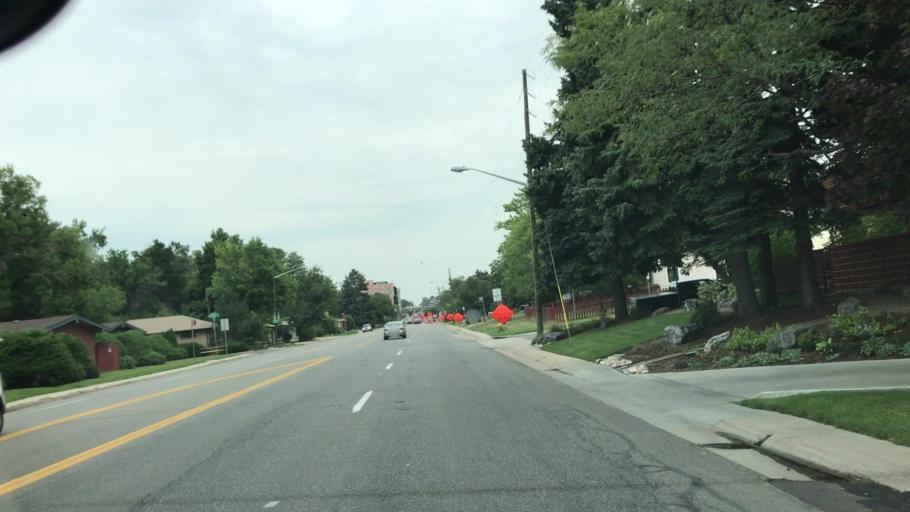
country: US
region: Colorado
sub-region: Arapahoe County
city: Cherry Hills Village
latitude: 39.6675
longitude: -104.9353
